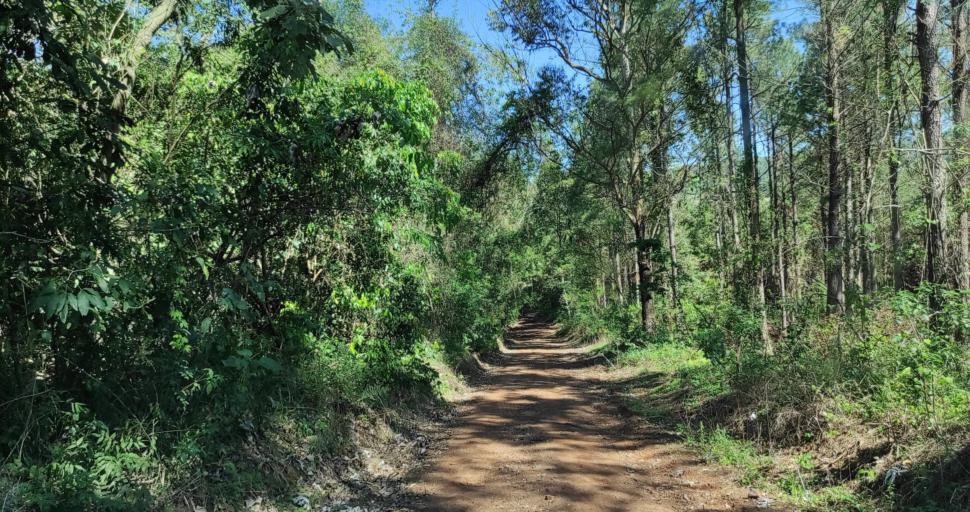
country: AR
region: Misiones
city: Ruiz de Montoya
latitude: -26.9486
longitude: -54.9808
